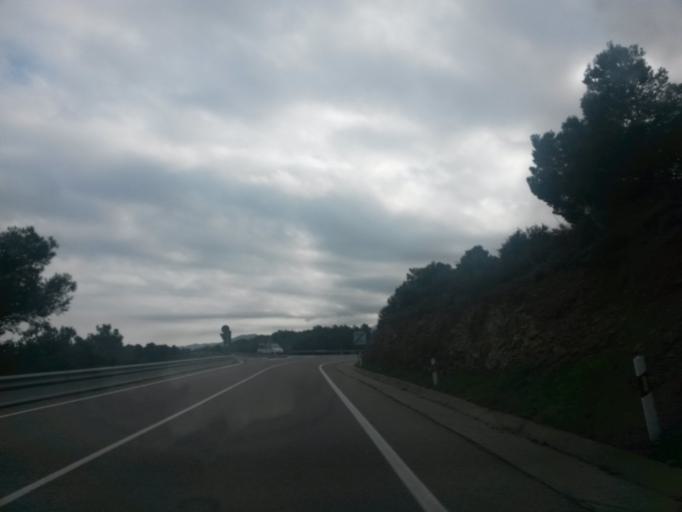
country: ES
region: Catalonia
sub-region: Provincia de Girona
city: Colera
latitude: 42.3891
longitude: 3.1574
